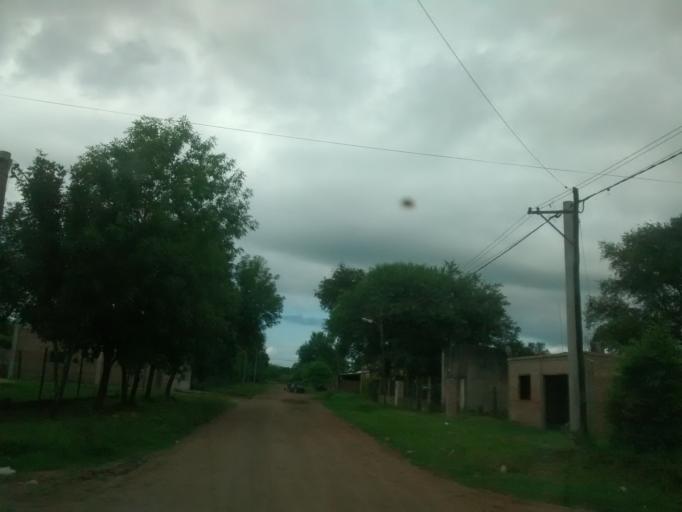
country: AR
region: Chaco
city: Puerto Tirol
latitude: -27.3832
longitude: -59.0873
